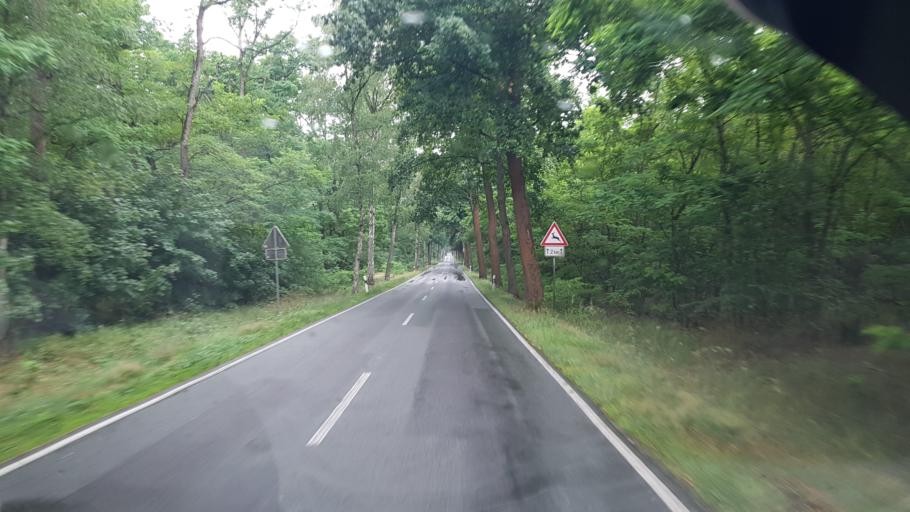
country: DE
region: Brandenburg
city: Schlieben
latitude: 51.7737
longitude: 13.3739
